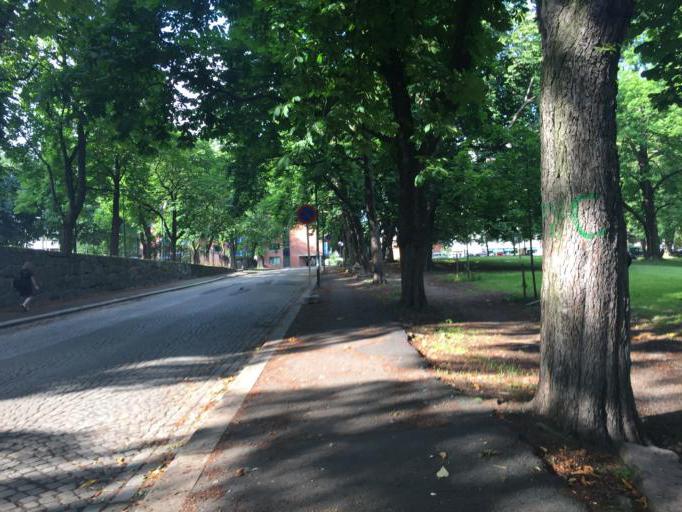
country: NO
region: Oslo
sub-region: Oslo
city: Oslo
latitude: 59.9221
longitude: 10.7665
